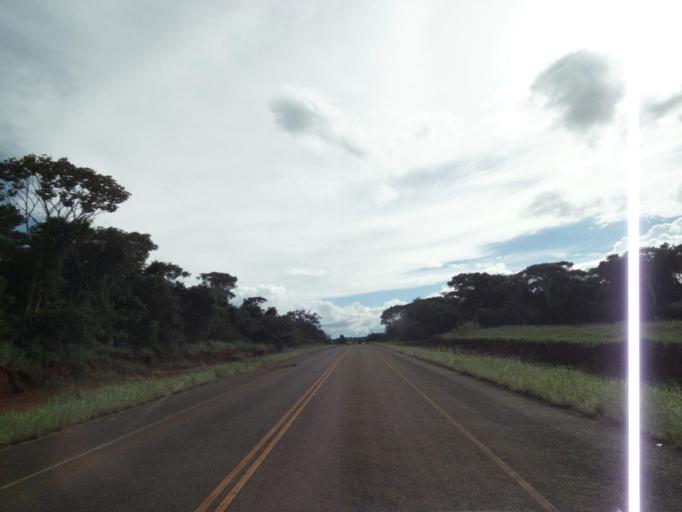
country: BR
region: Goias
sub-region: Jaragua
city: Jaragua
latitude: -15.8757
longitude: -49.4218
